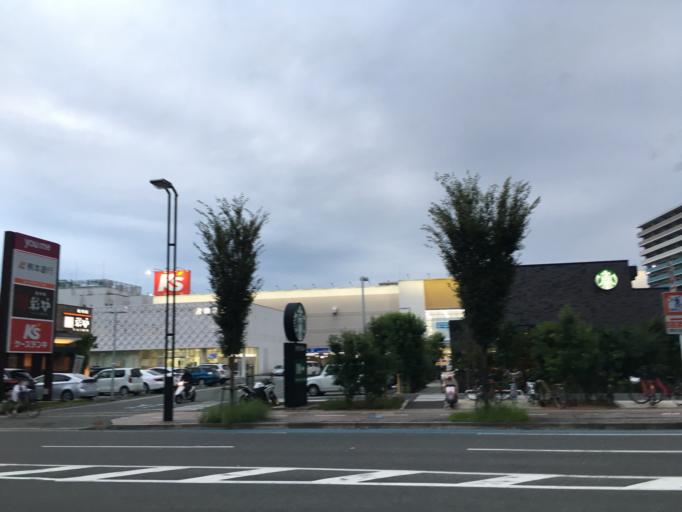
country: JP
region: Kumamoto
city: Kumamoto
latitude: 32.8043
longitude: 130.7263
